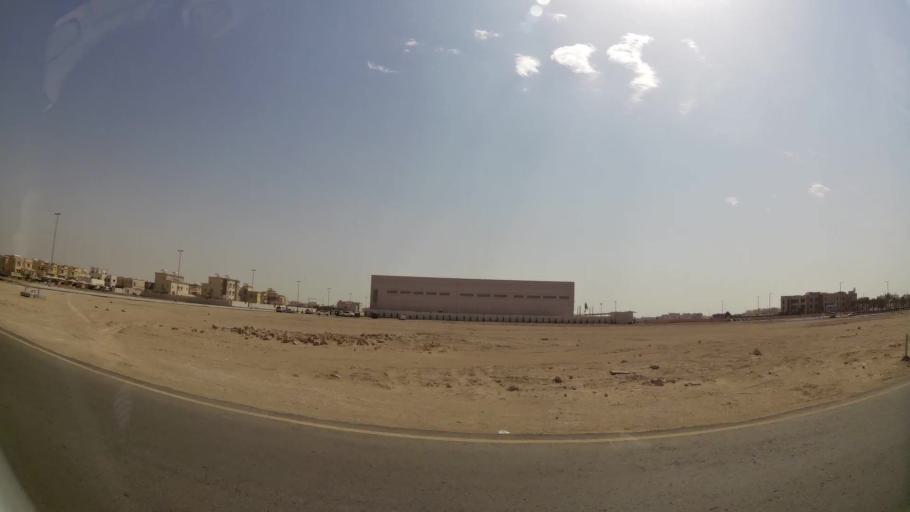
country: AE
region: Abu Dhabi
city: Abu Dhabi
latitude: 24.3415
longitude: 54.5569
